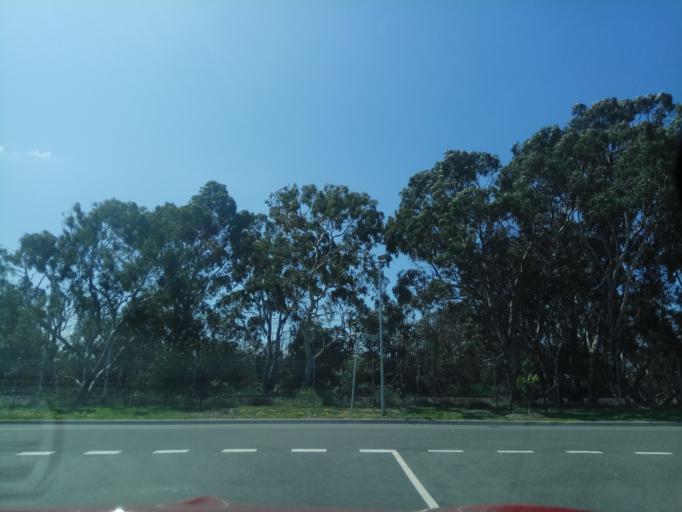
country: AU
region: Victoria
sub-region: Casey
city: Lynbrook
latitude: -38.0522
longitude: 145.2462
